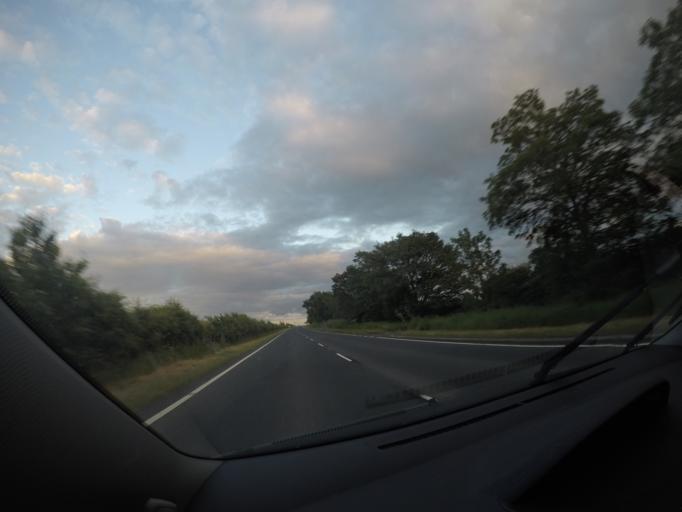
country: GB
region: England
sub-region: North Yorkshire
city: Ripon
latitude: 54.2328
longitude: -1.4948
